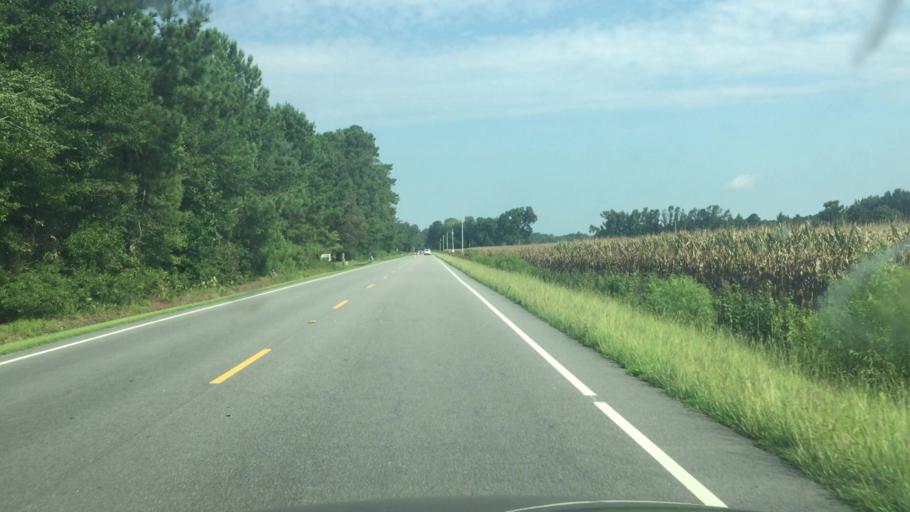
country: US
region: North Carolina
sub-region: Columbus County
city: Chadbourn
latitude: 34.2837
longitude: -78.8194
